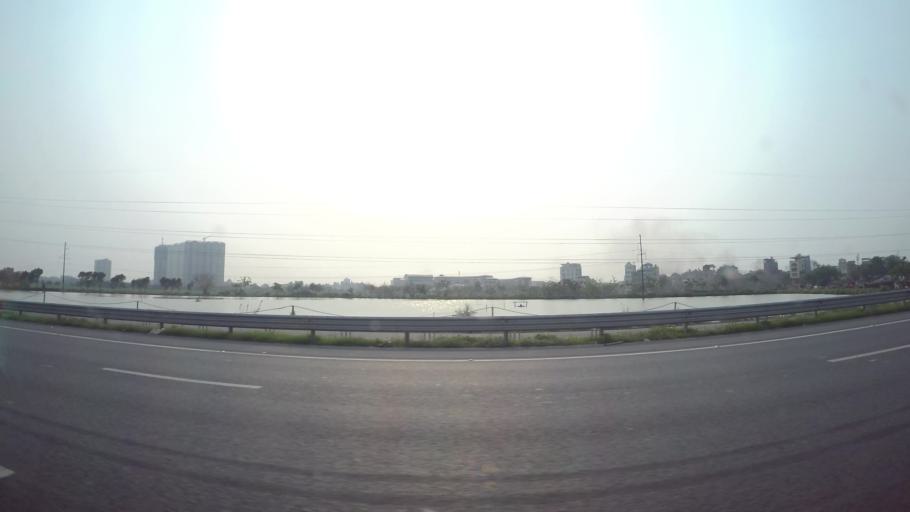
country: VN
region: Ha Noi
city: Van Dien
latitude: 20.9376
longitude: 105.8593
